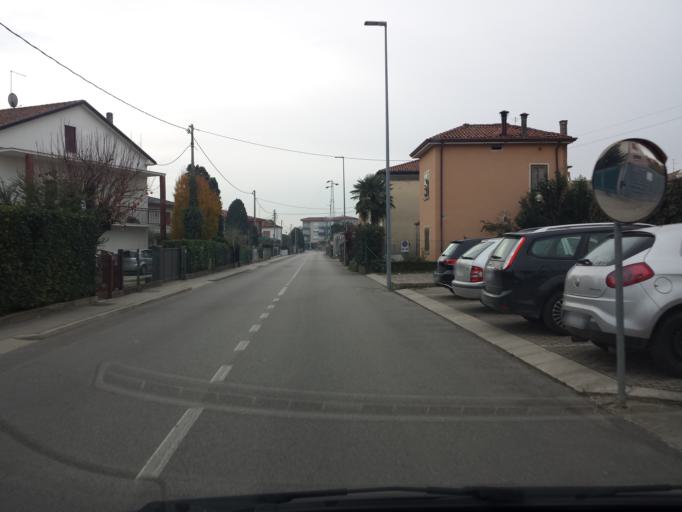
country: IT
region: Veneto
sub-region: Provincia di Vicenza
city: Sandrigo
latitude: 45.6656
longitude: 11.5969
